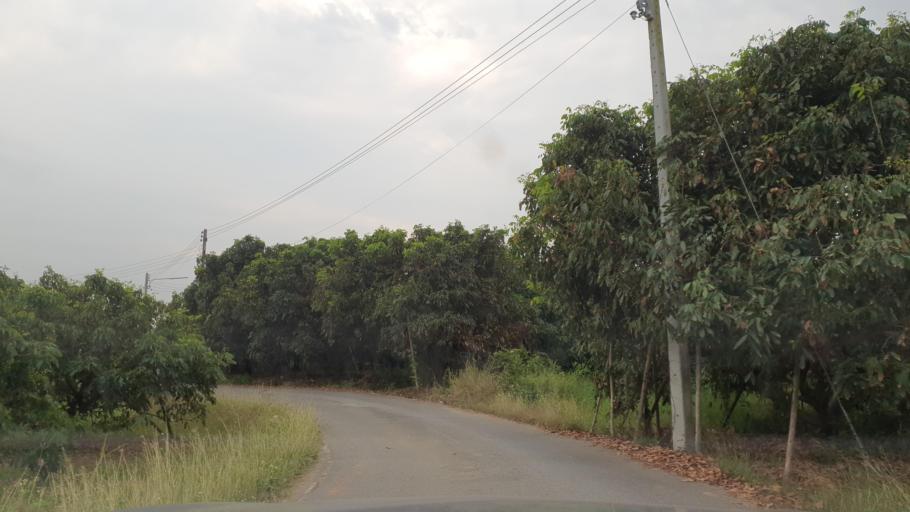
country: TH
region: Chiang Mai
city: Hang Dong
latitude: 18.6774
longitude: 98.9468
